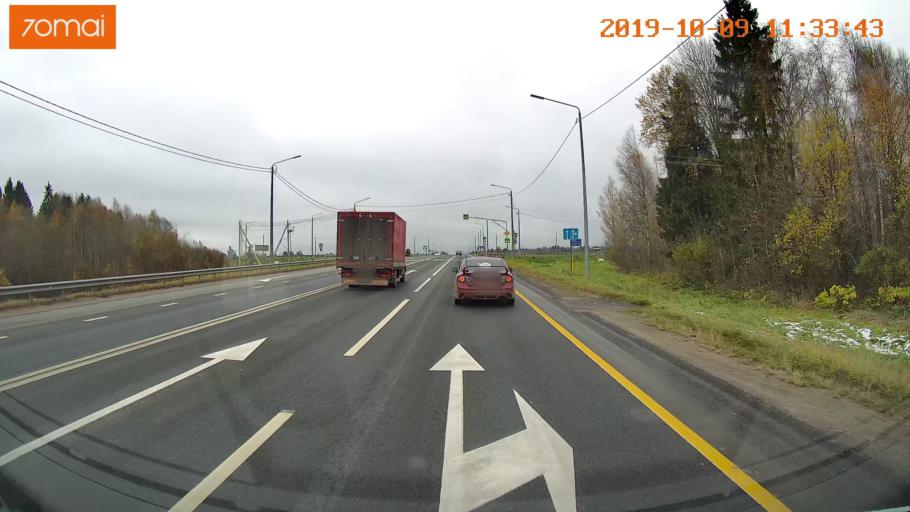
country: RU
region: Vologda
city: Gryazovets
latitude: 59.0222
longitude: 40.1151
